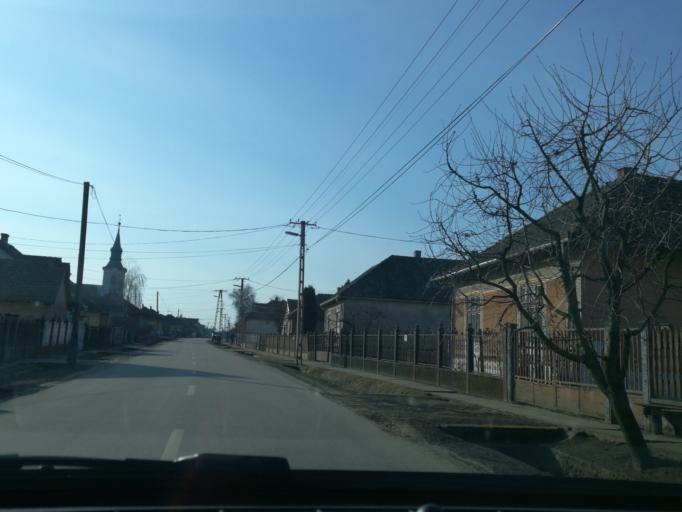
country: HU
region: Szabolcs-Szatmar-Bereg
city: Apagy
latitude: 48.0234
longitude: 21.9604
